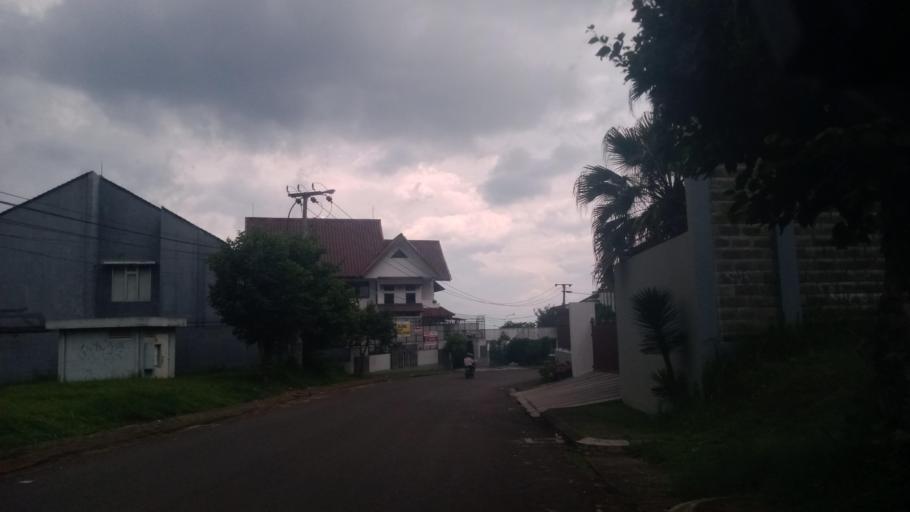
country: ID
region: West Java
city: Lembang
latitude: -6.8507
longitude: 107.5883
